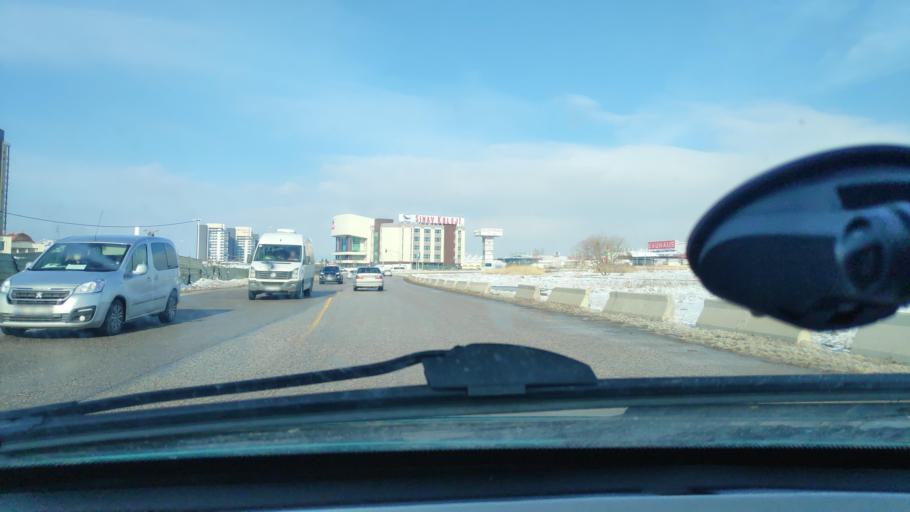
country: TR
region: Ankara
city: Ankara
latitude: 40.0138
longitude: 32.8294
